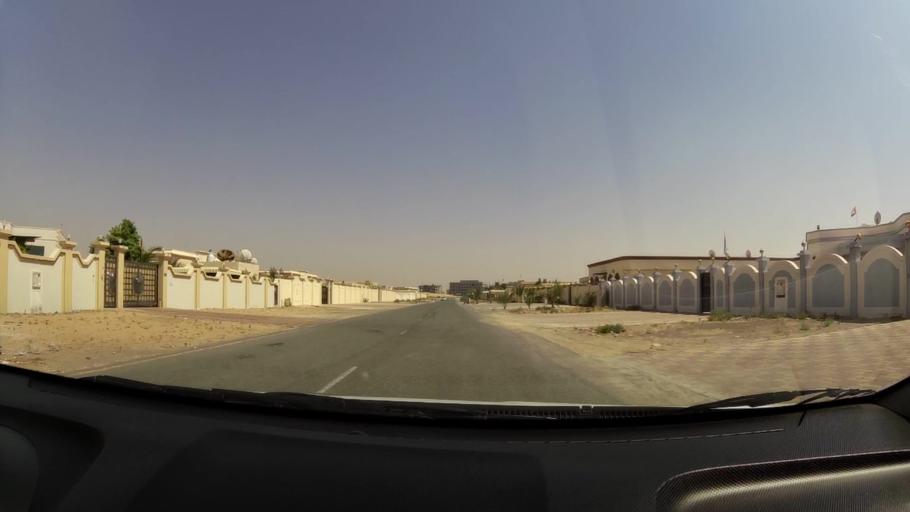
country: AE
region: Umm al Qaywayn
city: Umm al Qaywayn
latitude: 25.4848
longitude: 55.5860
